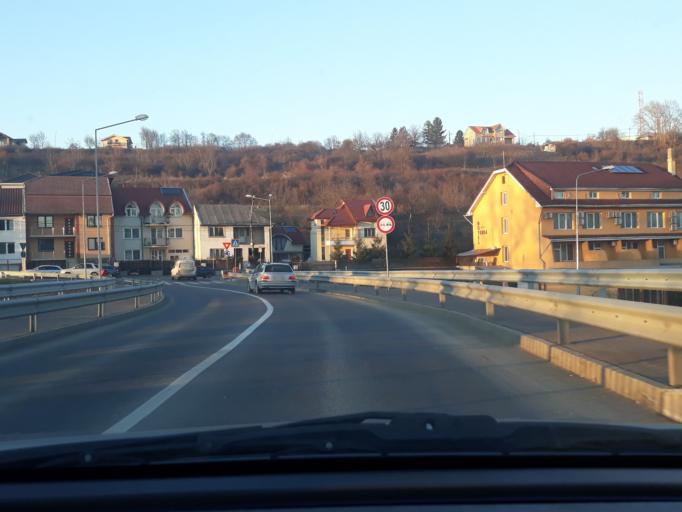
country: RO
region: Bihor
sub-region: Comuna Biharea
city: Oradea
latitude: 47.0518
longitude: 21.9605
